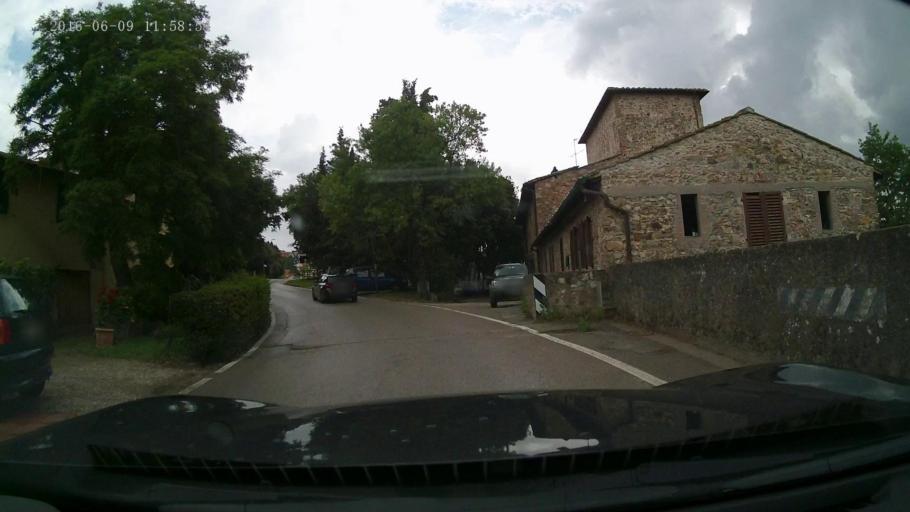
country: IT
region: Tuscany
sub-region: Province of Florence
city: Panzano in Chianti
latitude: 43.5455
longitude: 11.3096
